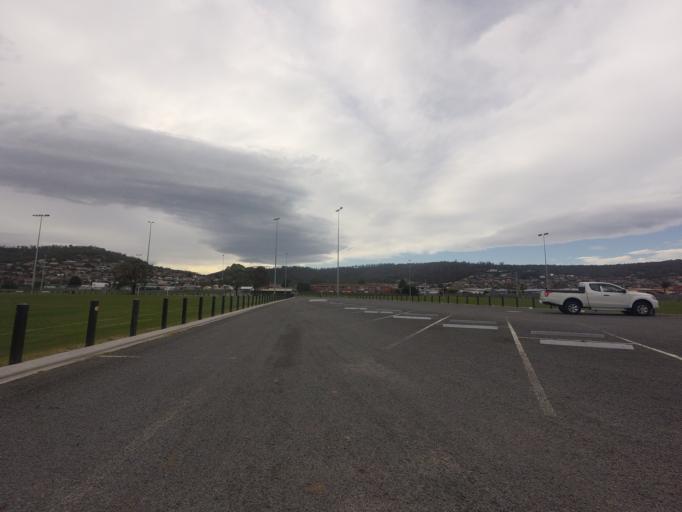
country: AU
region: Tasmania
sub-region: Clarence
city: Howrah
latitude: -42.8799
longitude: 147.3945
